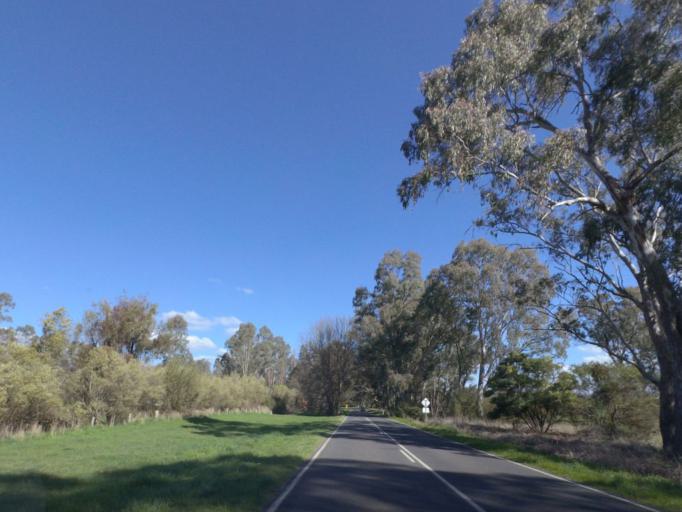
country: AU
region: Victoria
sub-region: Murrindindi
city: Alexandra
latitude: -37.2363
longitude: 145.7692
